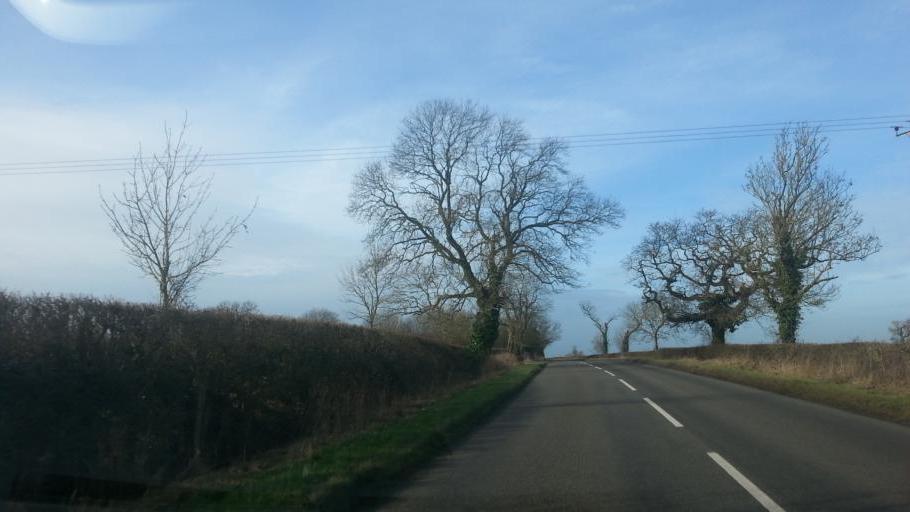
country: GB
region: England
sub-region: Leicestershire
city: Asfordby
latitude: 52.6795
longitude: -0.9467
